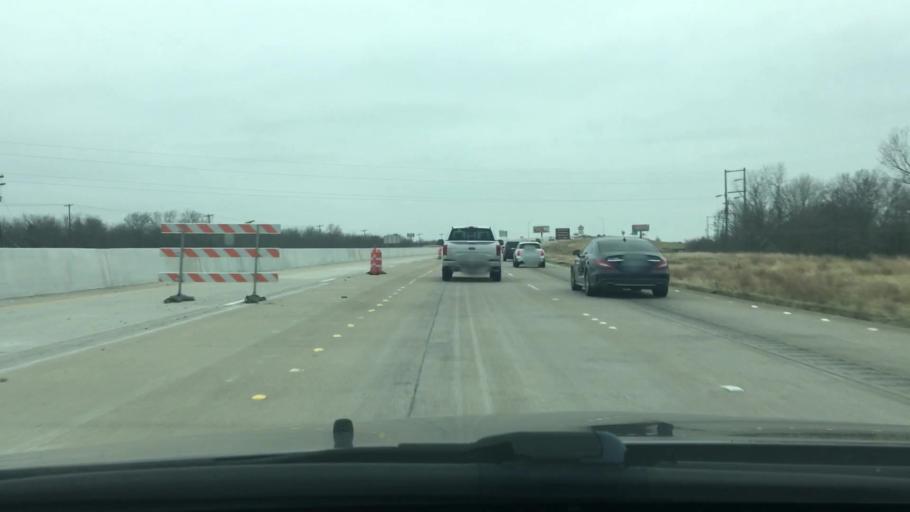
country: US
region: Texas
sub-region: Navarro County
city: Corsicana
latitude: 32.0820
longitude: -96.4400
